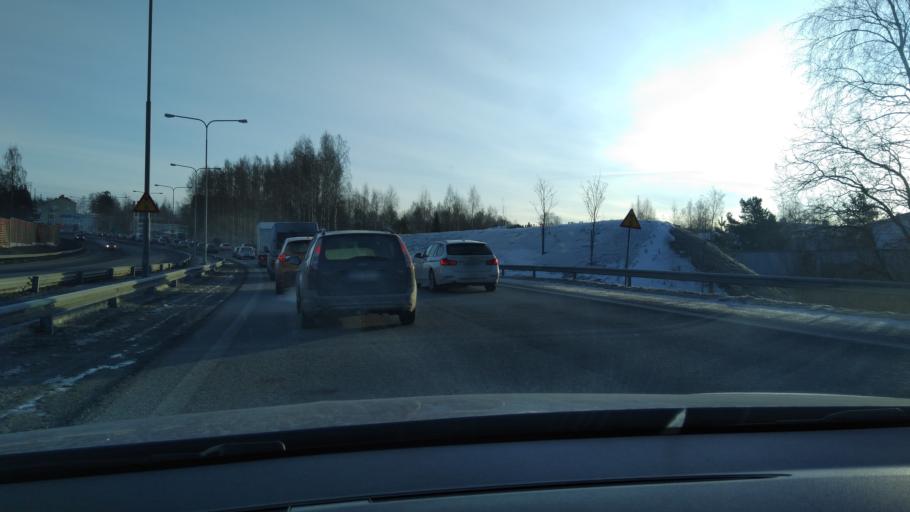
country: FI
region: Pirkanmaa
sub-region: Tampere
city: Pirkkala
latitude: 61.5056
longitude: 23.6846
